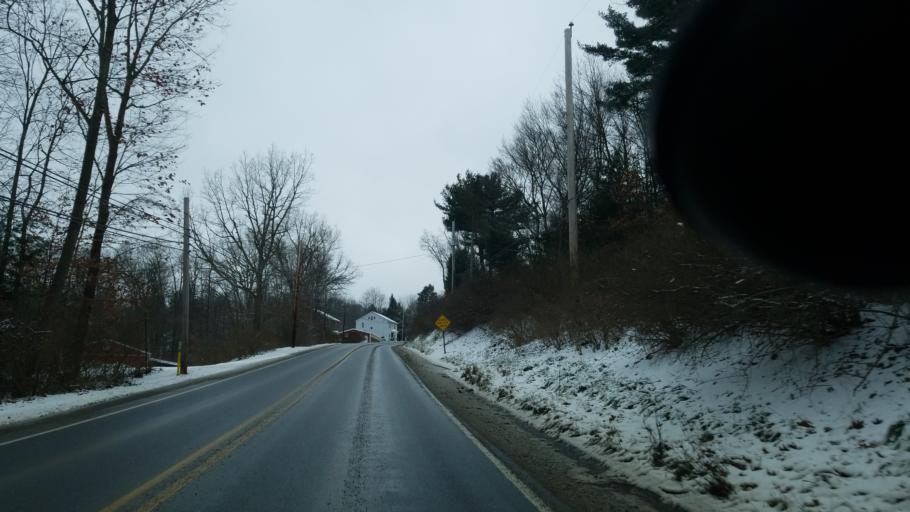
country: US
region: Pennsylvania
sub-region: Jefferson County
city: Albion
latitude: 40.9363
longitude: -78.9420
